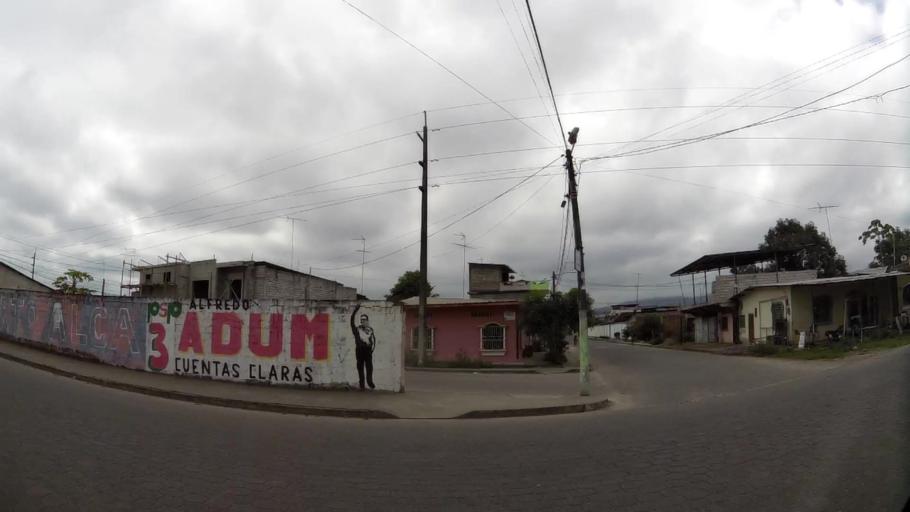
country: EC
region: Guayas
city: Naranjal
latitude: -2.6776
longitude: -79.6232
